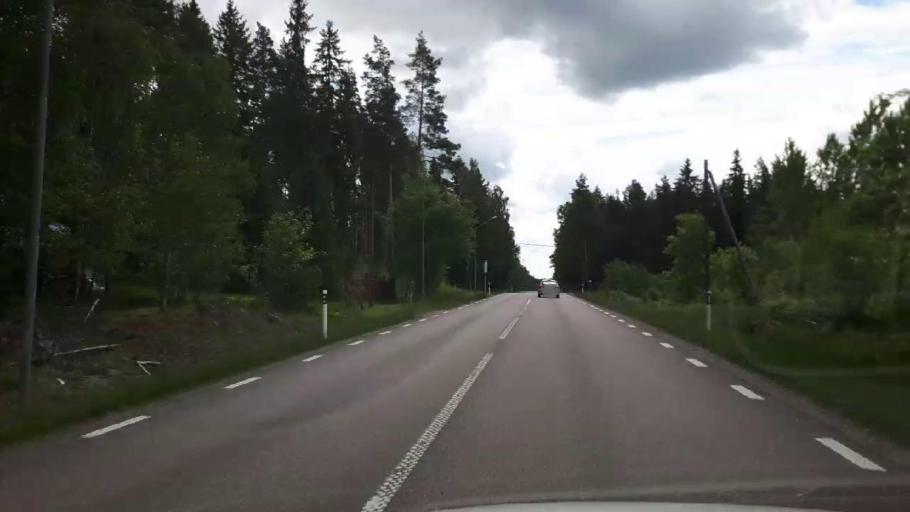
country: SE
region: Dalarna
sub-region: Faluns Kommun
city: Falun
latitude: 60.5180
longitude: 15.7346
